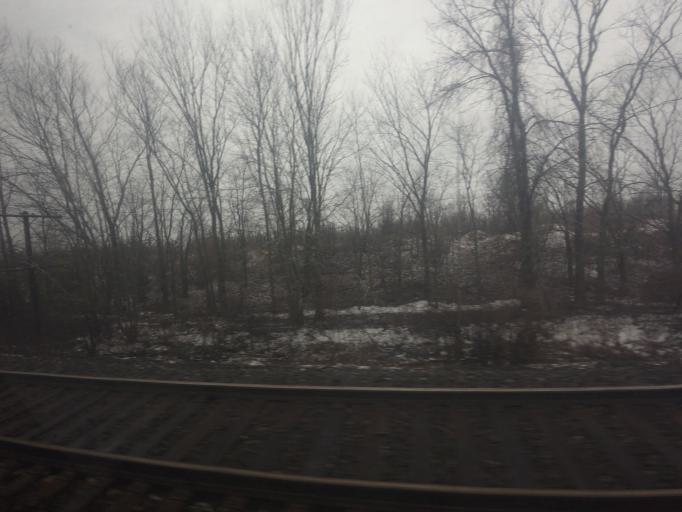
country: CA
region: Ontario
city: Kingston
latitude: 44.2276
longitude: -76.6635
